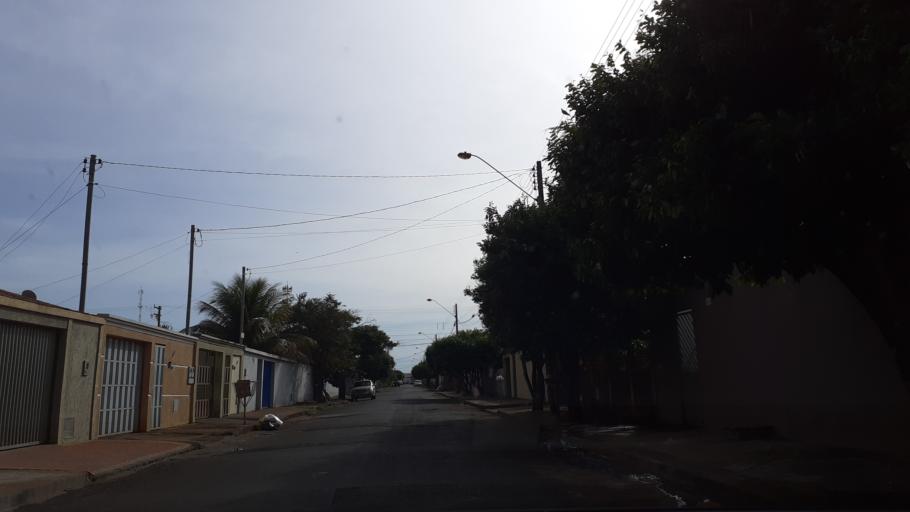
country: BR
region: Goias
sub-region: Itumbiara
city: Itumbiara
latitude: -18.4196
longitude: -49.2465
